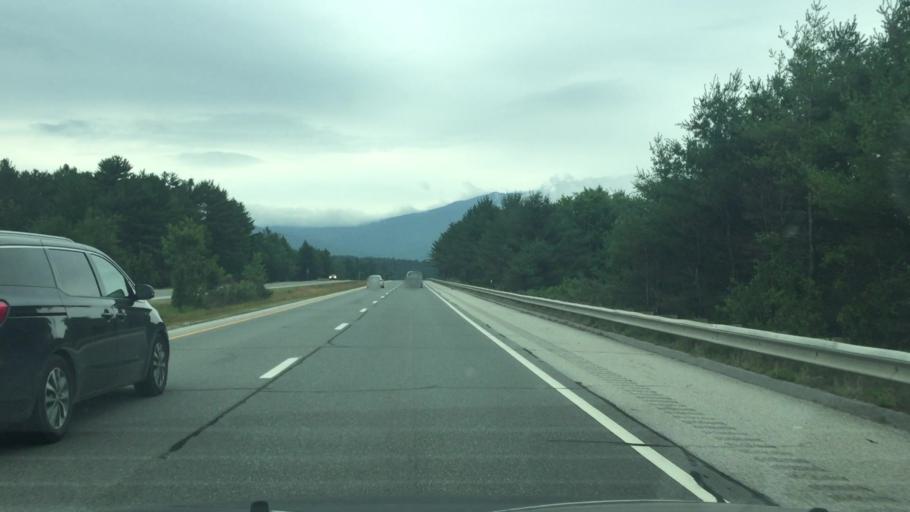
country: US
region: New Hampshire
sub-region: Grafton County
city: Littleton
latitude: 44.2244
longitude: -71.7378
